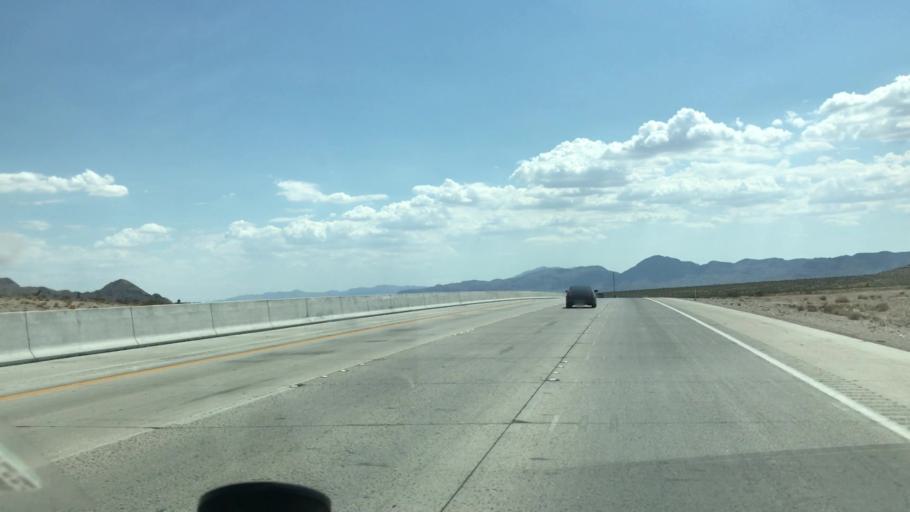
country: US
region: Nevada
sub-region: Clark County
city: Enterprise
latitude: 35.8290
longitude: -115.2913
